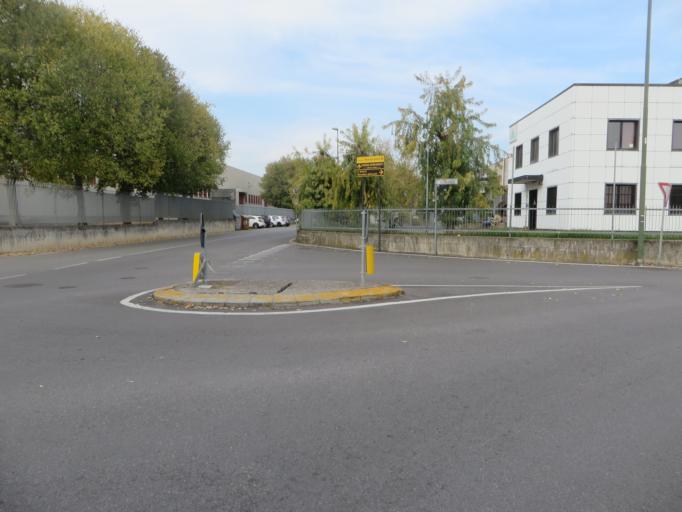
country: IT
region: Lombardy
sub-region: Provincia di Brescia
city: Castegnato
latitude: 45.5801
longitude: 10.1177
